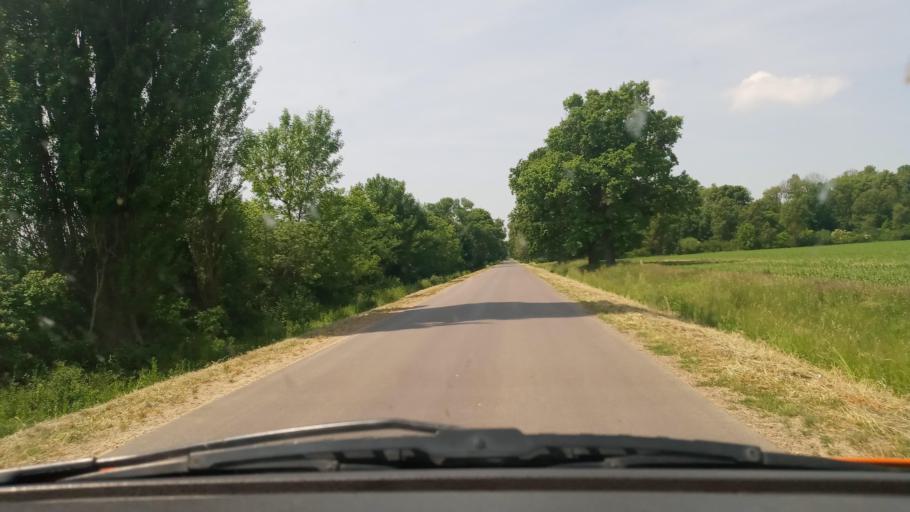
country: HU
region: Baranya
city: Szigetvar
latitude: 45.9675
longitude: 17.6763
